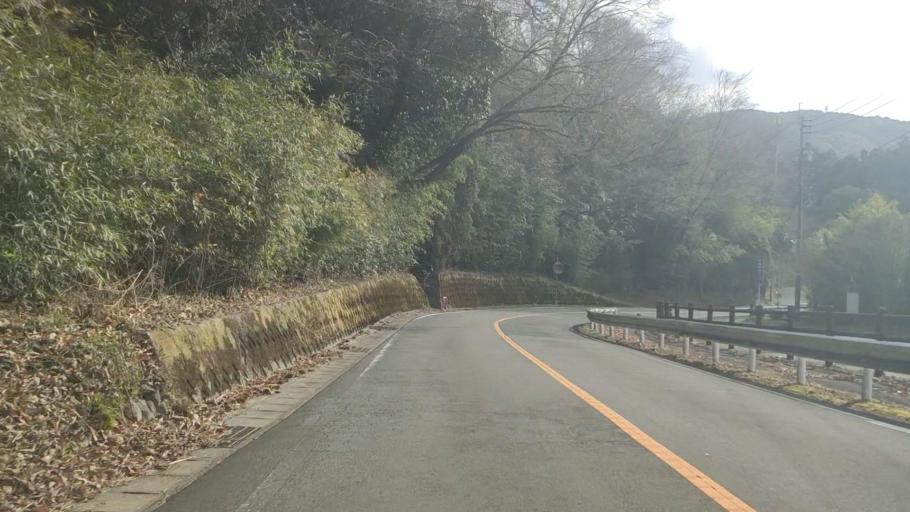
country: JP
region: Kumamoto
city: Hitoyoshi
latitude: 32.2906
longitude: 130.8443
